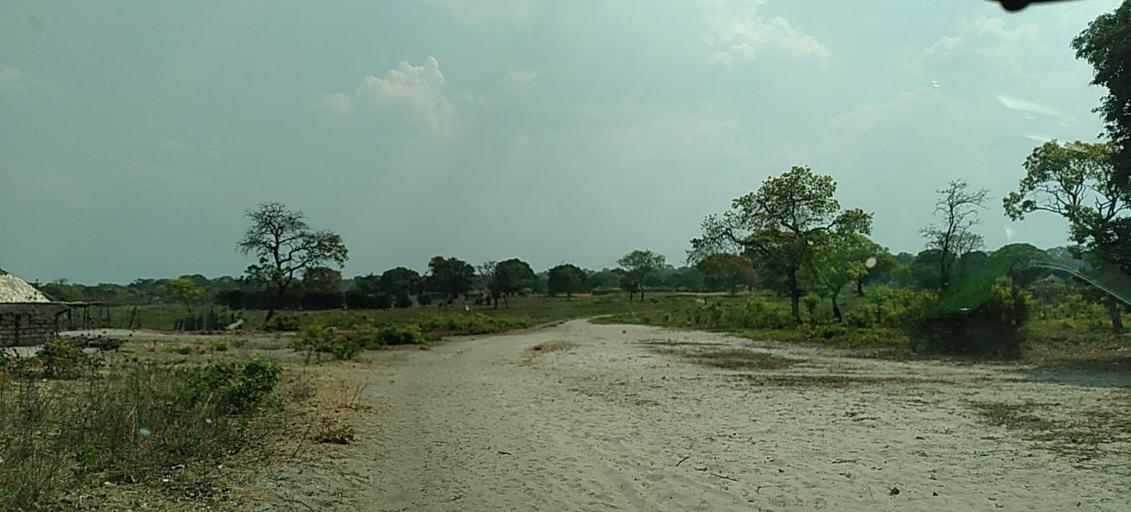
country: ZM
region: North-Western
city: Kabompo
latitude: -13.4471
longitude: 23.6651
